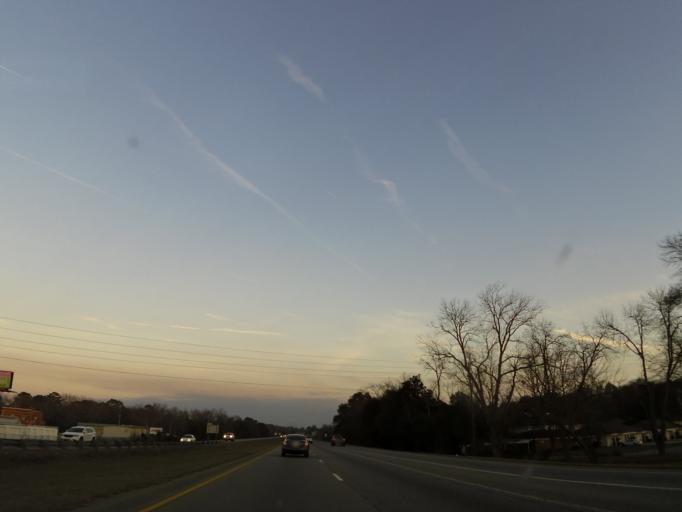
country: US
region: Georgia
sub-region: Dougherty County
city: Albany
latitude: 31.6150
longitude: -84.1725
